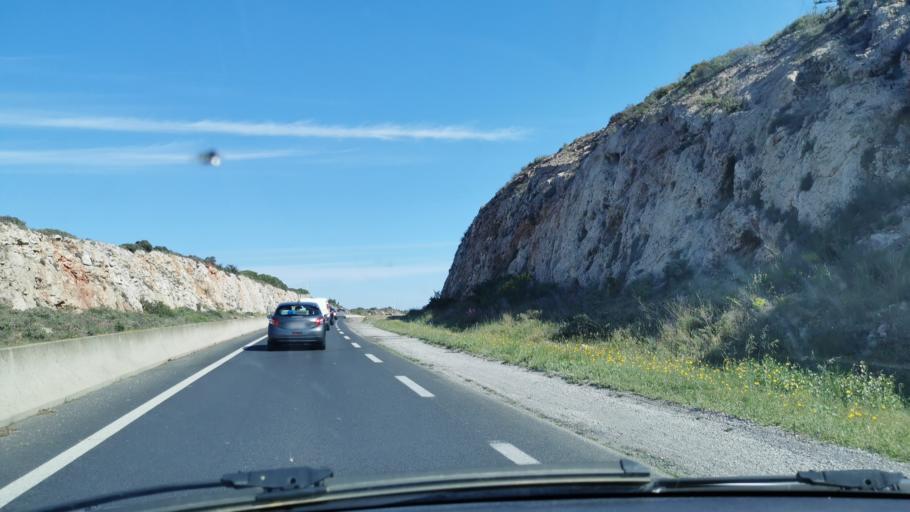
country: FR
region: Languedoc-Roussillon
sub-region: Departement de l'Herault
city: Balaruc-le-Vieux
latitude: 43.4490
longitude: 3.7072
